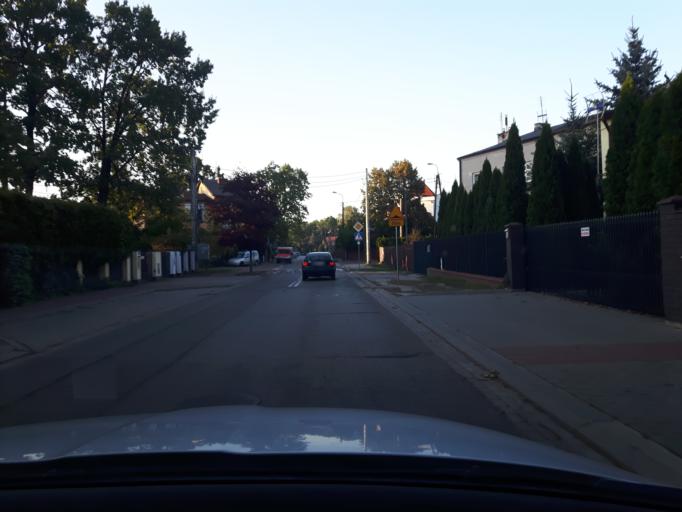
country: PL
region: Masovian Voivodeship
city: Zielonka
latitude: 52.3016
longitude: 21.1525
